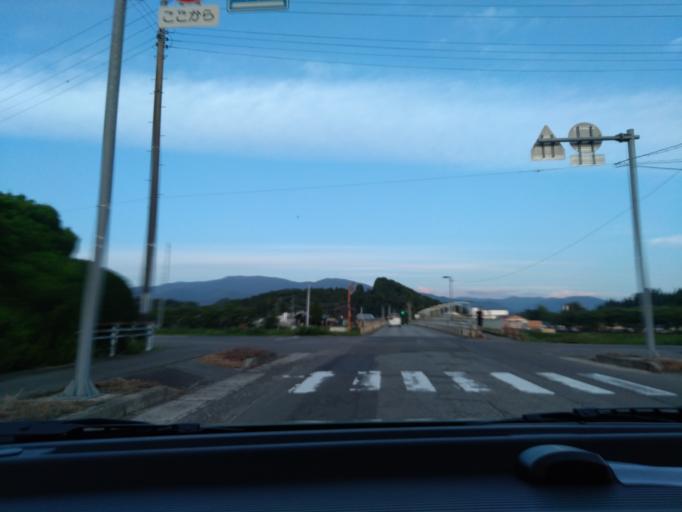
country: JP
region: Akita
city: Kakunodatemachi
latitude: 39.5919
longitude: 140.5572
